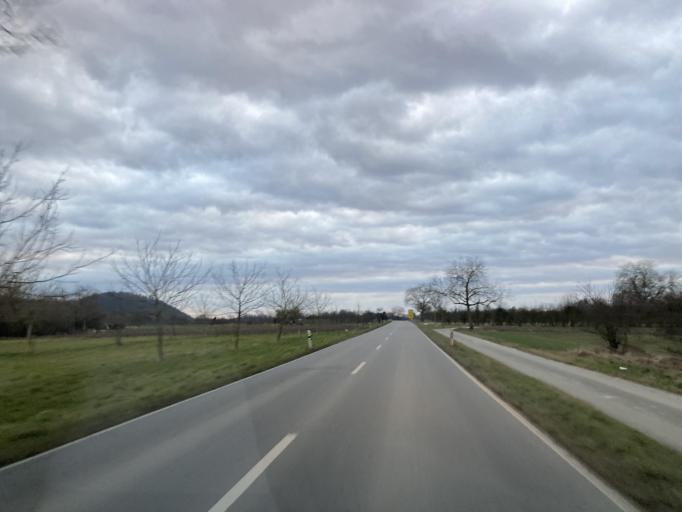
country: DE
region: Baden-Wuerttemberg
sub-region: Freiburg Region
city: Vogtsburg
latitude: 48.0893
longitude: 7.6032
